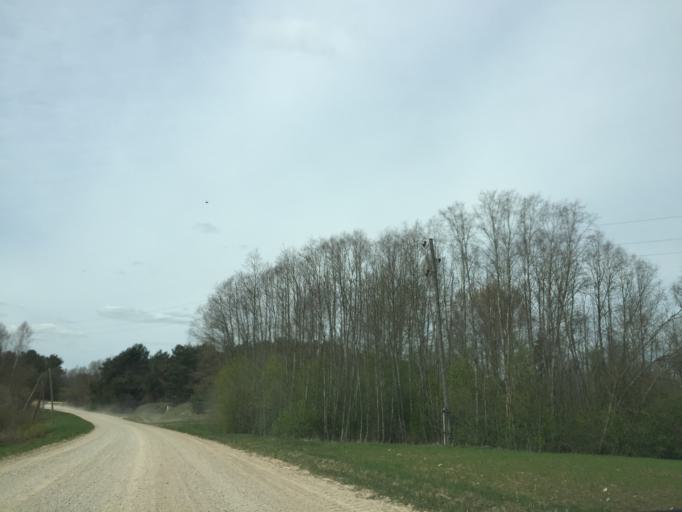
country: LV
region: Ludzas Rajons
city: Ludza
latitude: 56.5649
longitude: 27.5517
